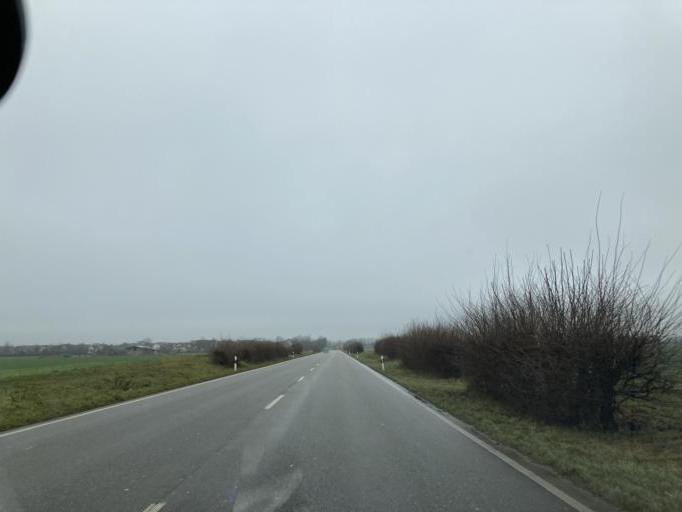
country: DE
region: Baden-Wuerttemberg
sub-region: Freiburg Region
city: Neuenburg am Rhein
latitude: 47.8177
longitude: 7.5797
